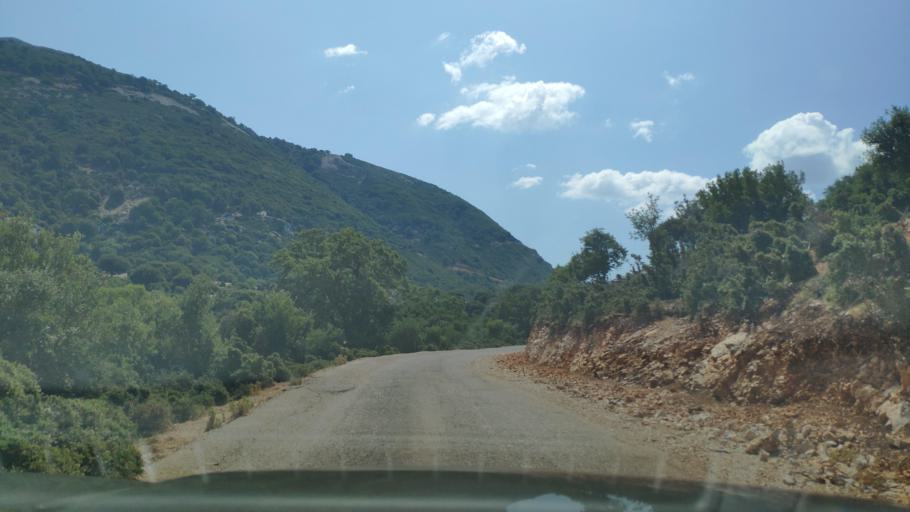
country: GR
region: West Greece
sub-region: Nomos Aitolias kai Akarnanias
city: Monastirakion
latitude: 38.8217
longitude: 20.9297
